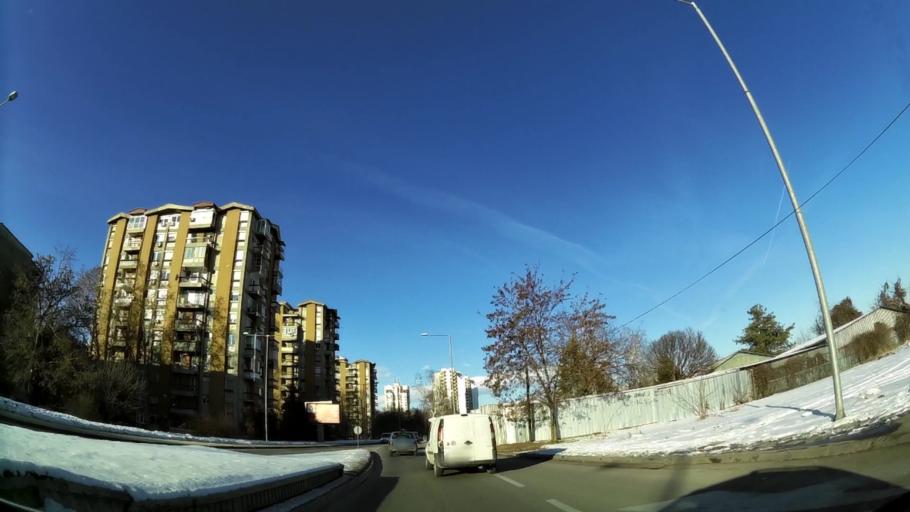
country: MK
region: Karpos
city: Skopje
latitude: 42.0081
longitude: 21.3903
